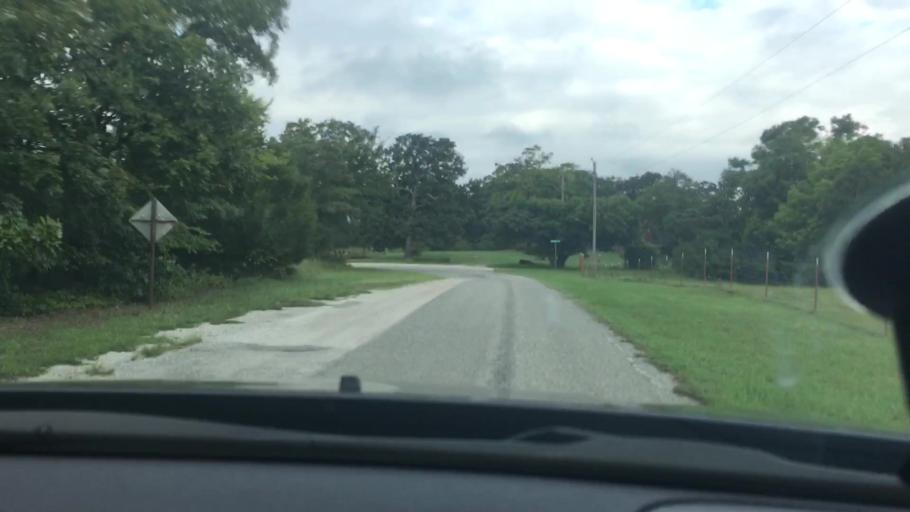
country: US
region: Oklahoma
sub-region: Pontotoc County
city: Byng
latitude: 34.8181
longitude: -96.5466
